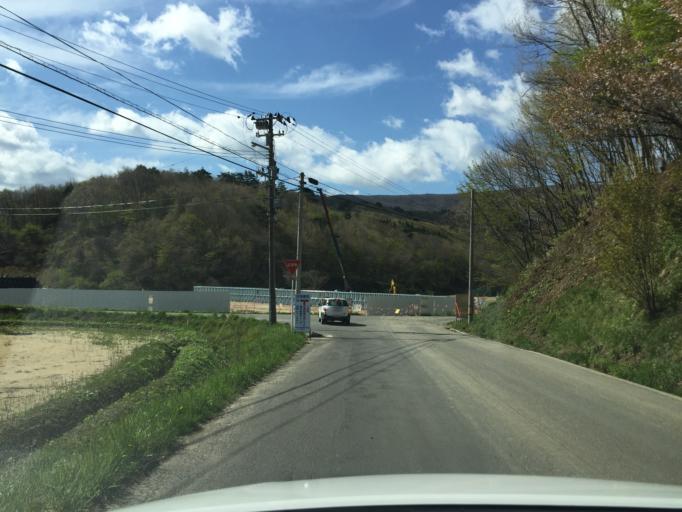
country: JP
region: Fukushima
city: Funehikimachi-funehiki
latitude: 37.5688
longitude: 140.6933
